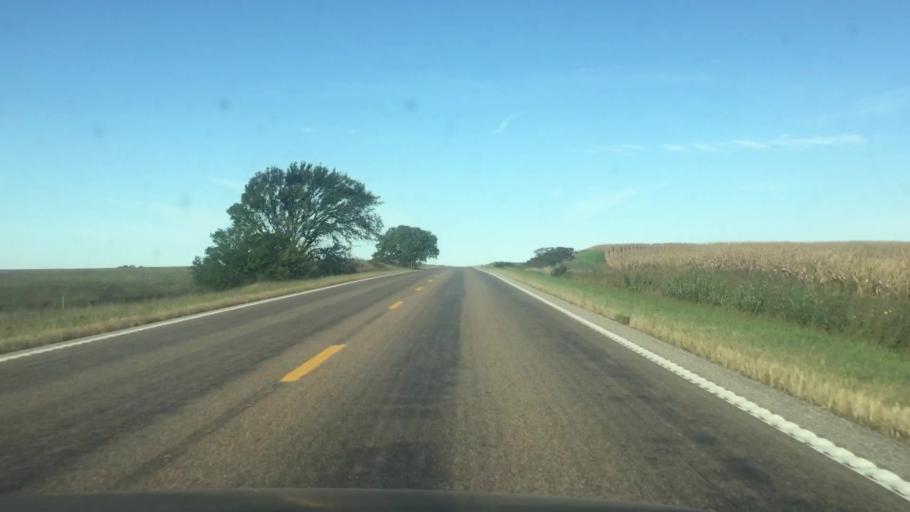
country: US
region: Nebraska
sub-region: Thayer County
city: Hebron
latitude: 40.1475
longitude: -97.4740
